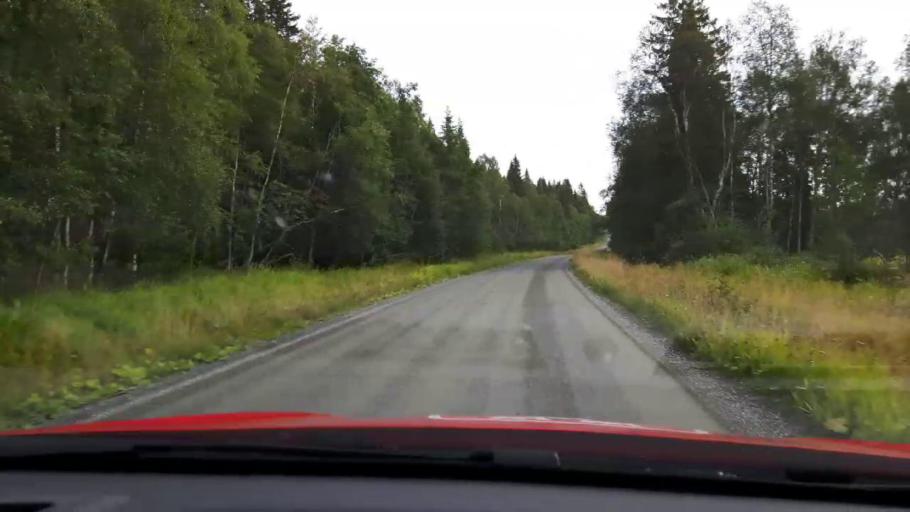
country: SE
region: Jaemtland
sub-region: Are Kommun
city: Are
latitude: 63.7414
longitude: 13.0025
